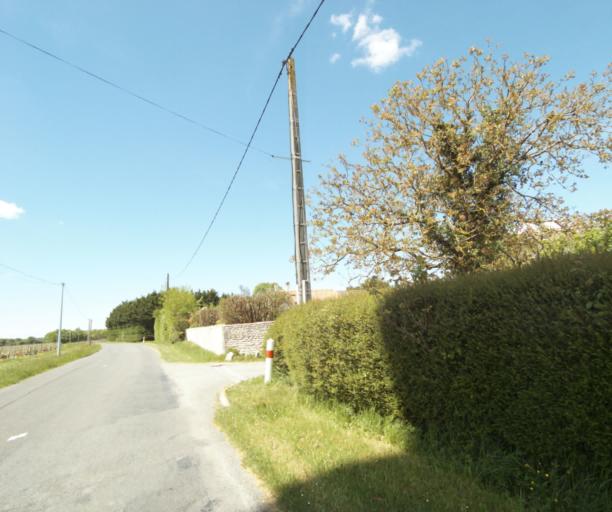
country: FR
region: Poitou-Charentes
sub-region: Departement de la Charente-Maritime
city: Burie
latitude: 45.7619
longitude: -0.4747
